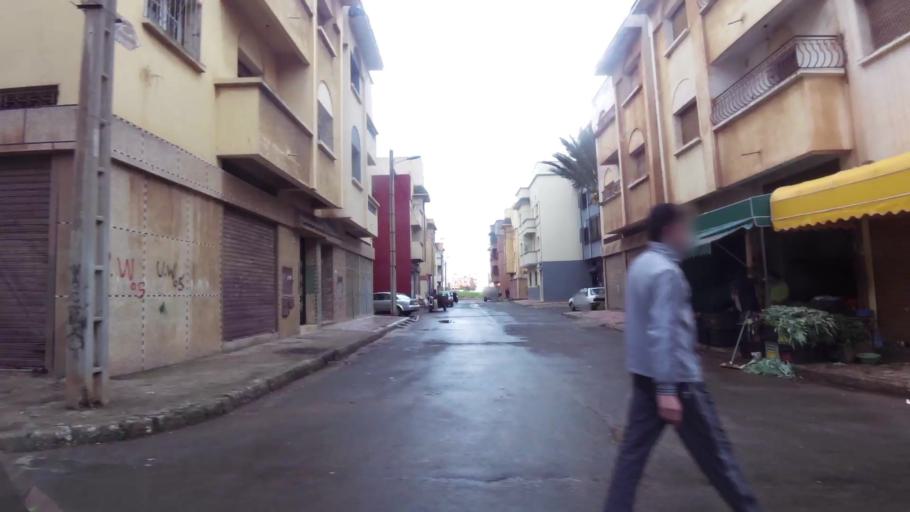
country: MA
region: Grand Casablanca
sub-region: Nouaceur
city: Bouskoura
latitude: 33.5072
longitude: -7.6532
